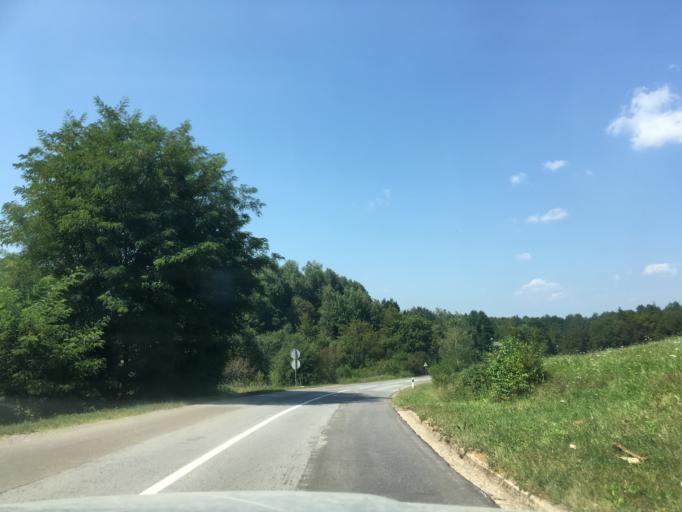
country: HR
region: Karlovacka
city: Ozalj
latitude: 45.5178
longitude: 15.3945
